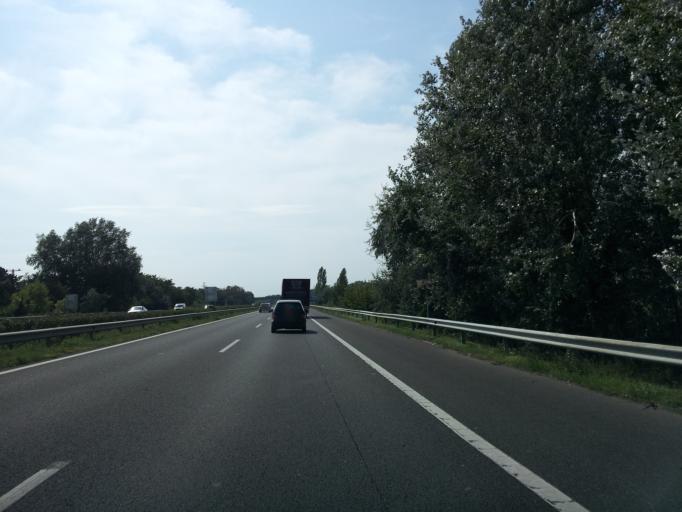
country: HU
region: Fejer
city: Velence
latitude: 47.2458
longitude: 18.6467
